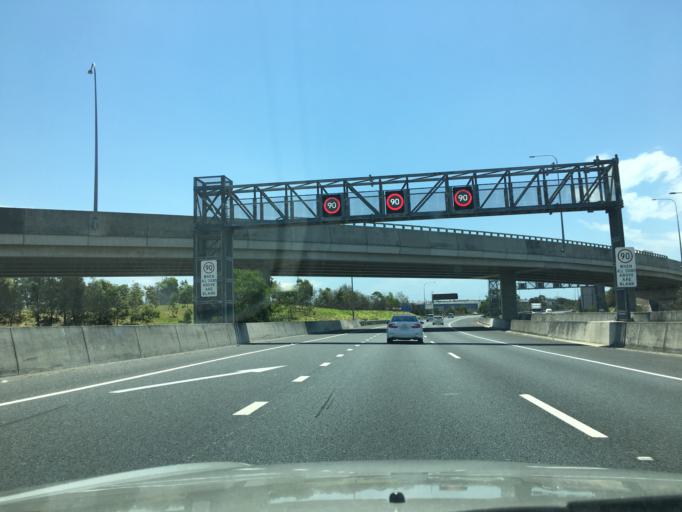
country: AU
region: Queensland
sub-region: Brisbane
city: Wavell Heights
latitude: -27.3935
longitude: 153.0930
